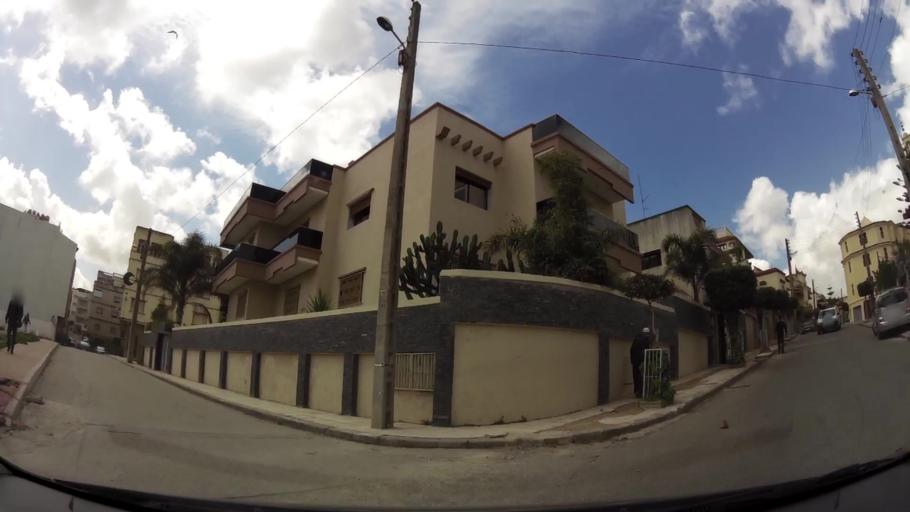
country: MA
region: Tanger-Tetouan
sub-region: Tanger-Assilah
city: Tangier
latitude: 35.7615
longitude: -5.8133
